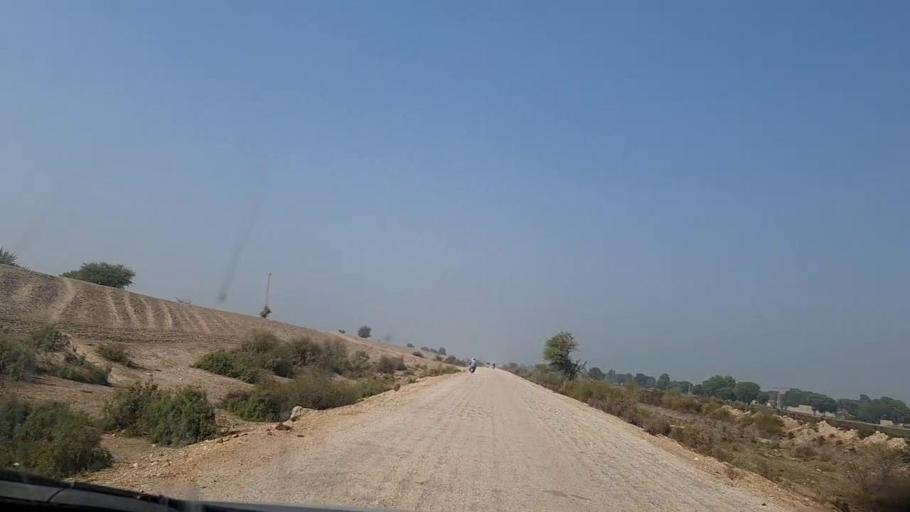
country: PK
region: Sindh
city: Moro
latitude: 26.7180
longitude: 67.9234
